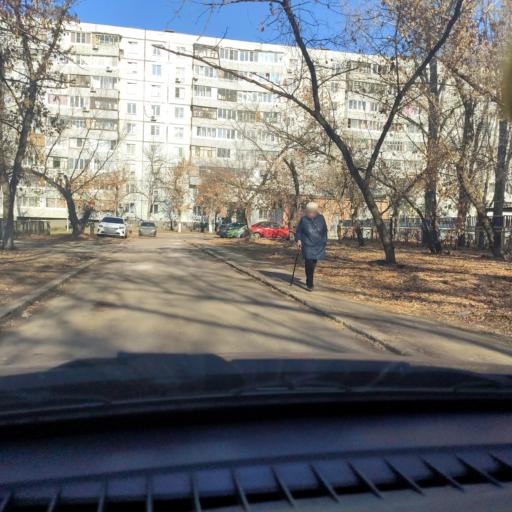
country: RU
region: Samara
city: Tol'yatti
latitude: 53.5355
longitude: 49.2938
